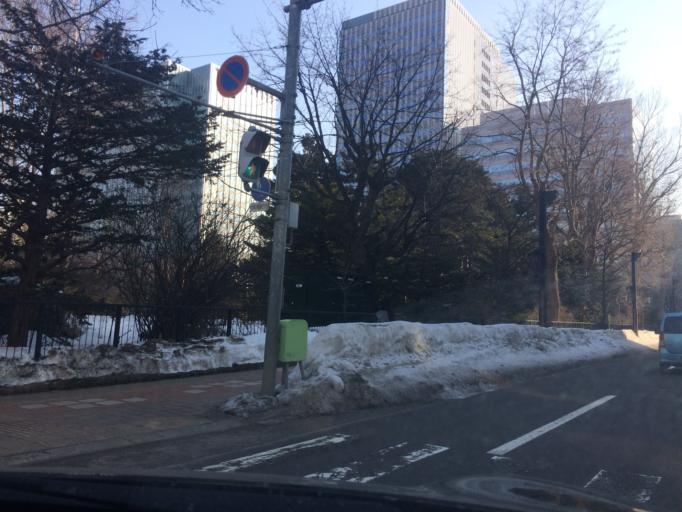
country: JP
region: Hokkaido
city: Sapporo
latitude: 43.0627
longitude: 141.3483
